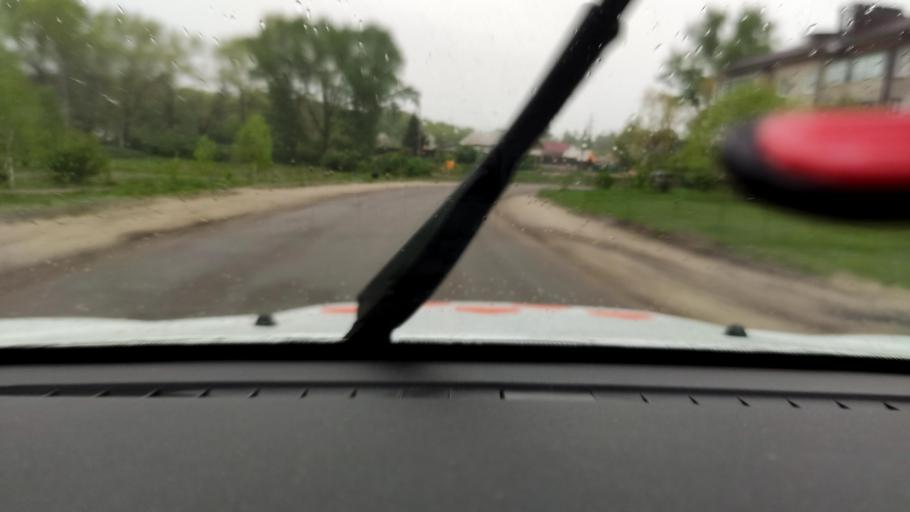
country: RU
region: Voronezj
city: Strelitsa
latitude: 51.6102
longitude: 38.8981
